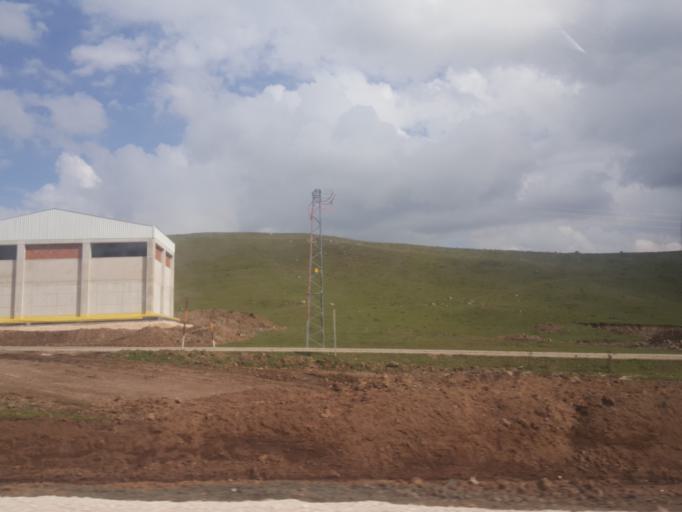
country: TR
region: Tokat
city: Bereketli
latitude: 40.5648
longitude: 37.3043
